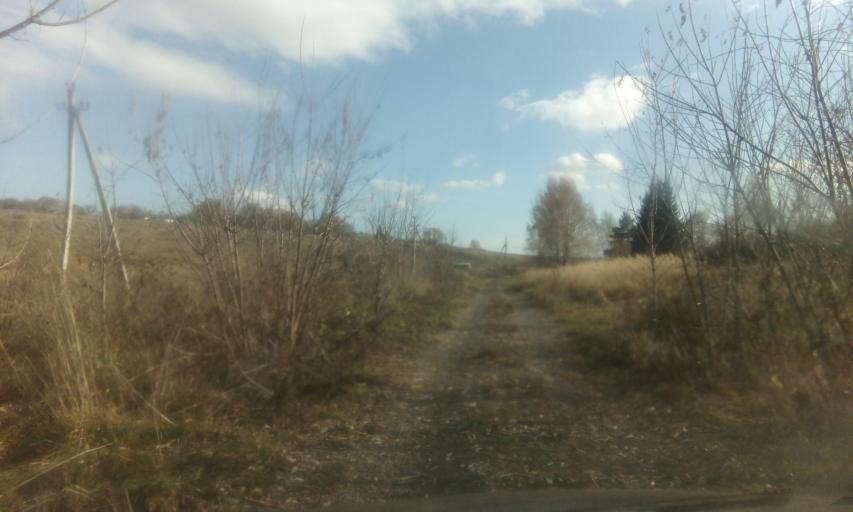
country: RU
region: Tula
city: Dubovka
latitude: 53.9163
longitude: 38.0659
